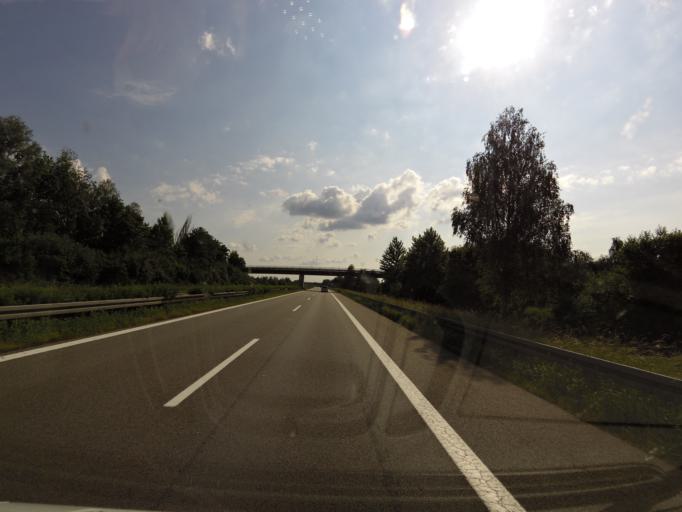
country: DE
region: Bavaria
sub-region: Lower Bavaria
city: Landau an der Isar
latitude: 48.7107
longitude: 12.6999
